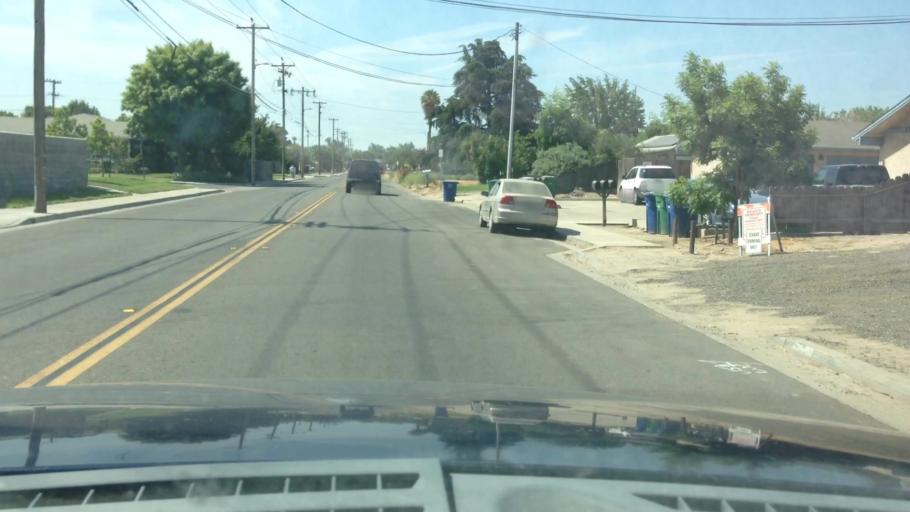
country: US
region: California
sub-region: Fresno County
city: Kingsburg
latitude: 36.5230
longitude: -119.5570
